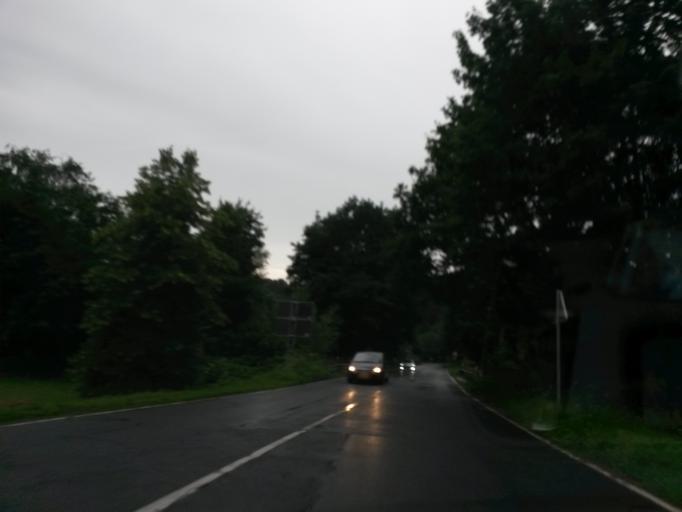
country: DE
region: North Rhine-Westphalia
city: Lohmar
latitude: 50.8650
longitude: 7.2473
